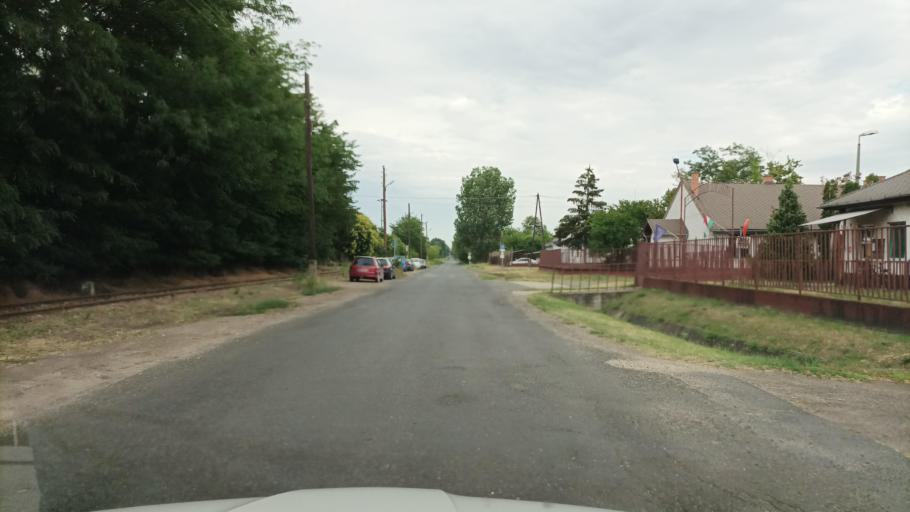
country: HU
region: Pest
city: Taborfalva
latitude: 47.0834
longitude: 19.4521
